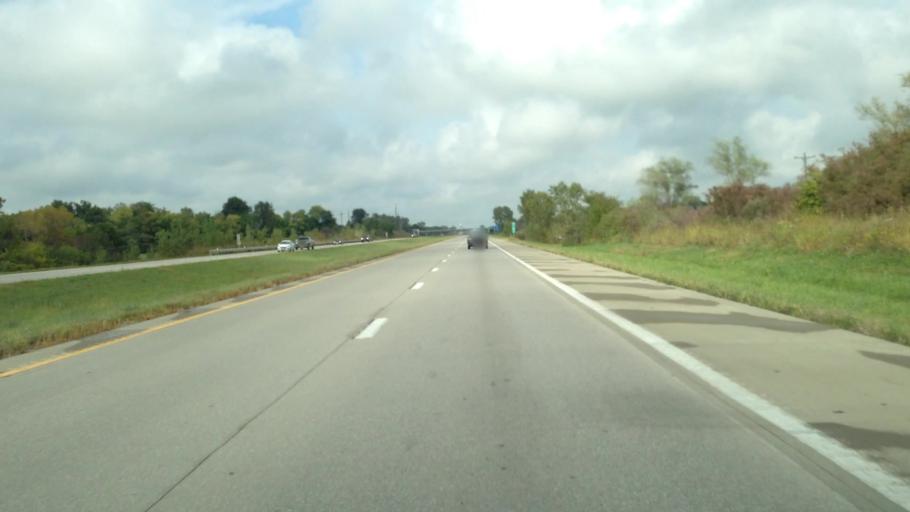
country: US
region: Missouri
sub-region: Clay County
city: Kearney
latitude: 39.4291
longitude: -94.3387
